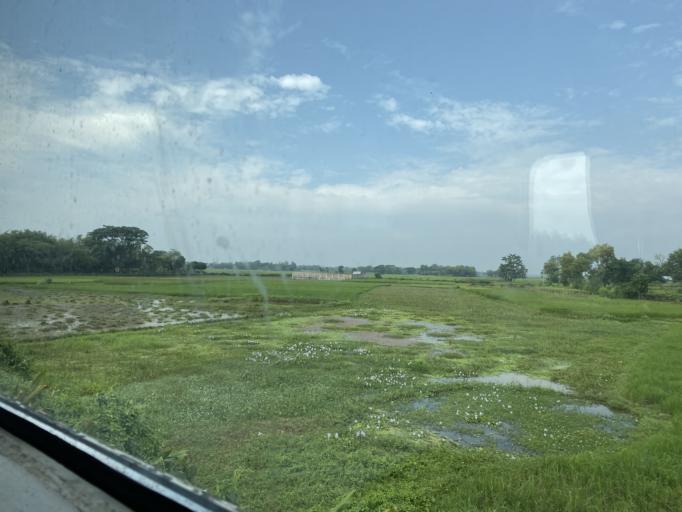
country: IN
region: Tripura
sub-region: West Tripura
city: Agartala
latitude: 23.9969
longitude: 91.2890
